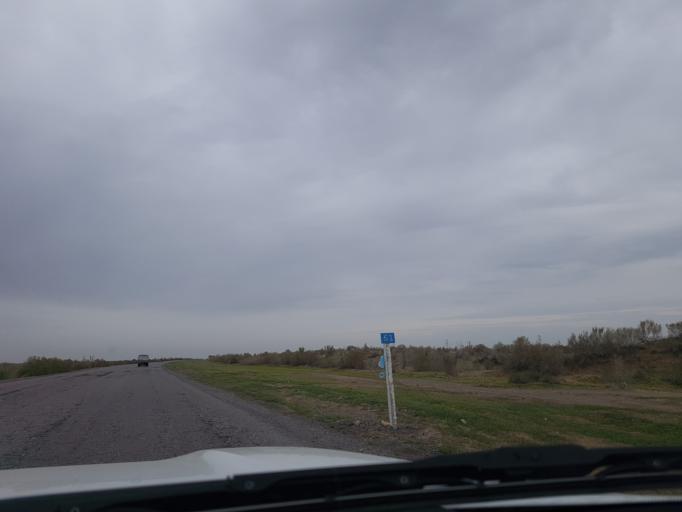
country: TM
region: Lebap
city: Turkmenabat
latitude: 38.8468
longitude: 63.4024
